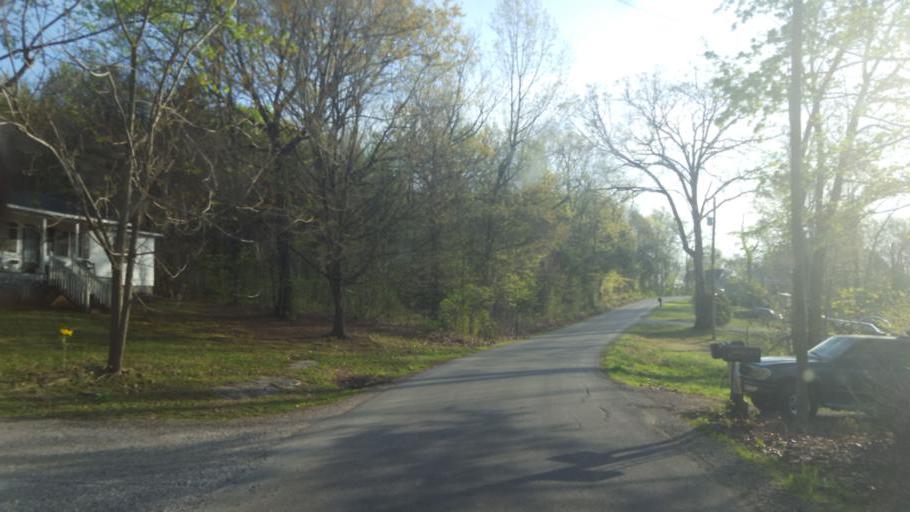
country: US
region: Kentucky
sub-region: Hart County
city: Munfordville
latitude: 37.2449
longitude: -85.9023
